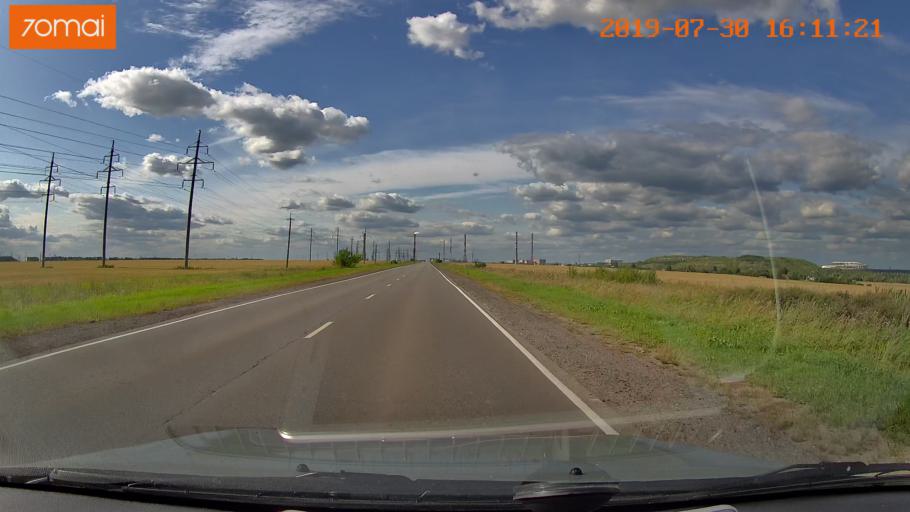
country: RU
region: Moskovskaya
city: Lopatinskiy
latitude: 55.2747
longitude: 38.7116
